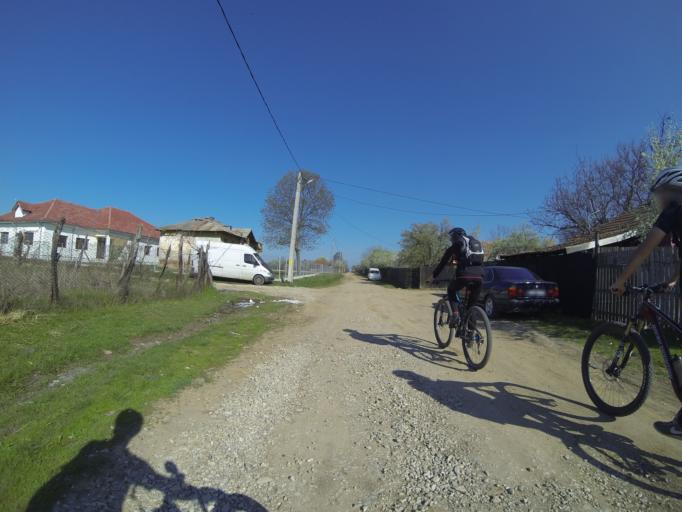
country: RO
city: Varvoru
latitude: 44.2256
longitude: 23.6528
